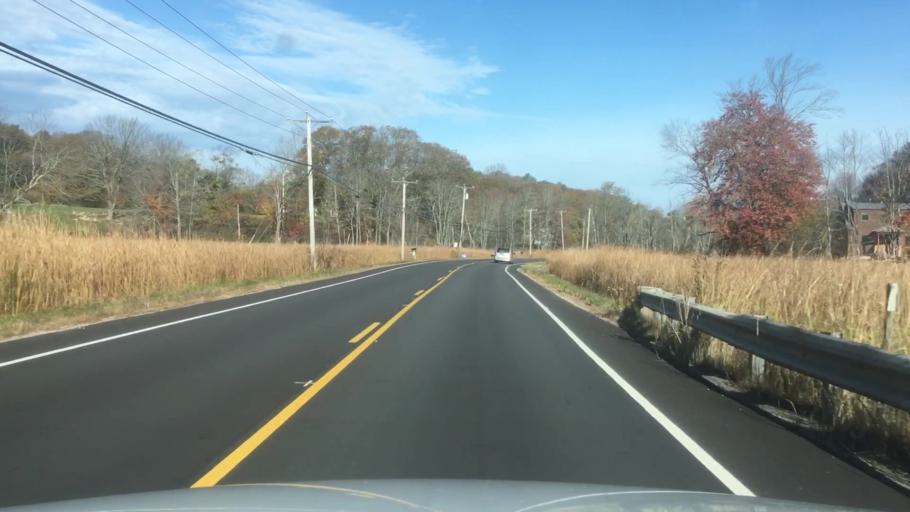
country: US
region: Maine
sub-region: Sagadahoc County
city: Woolwich
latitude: 43.9028
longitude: -69.7972
